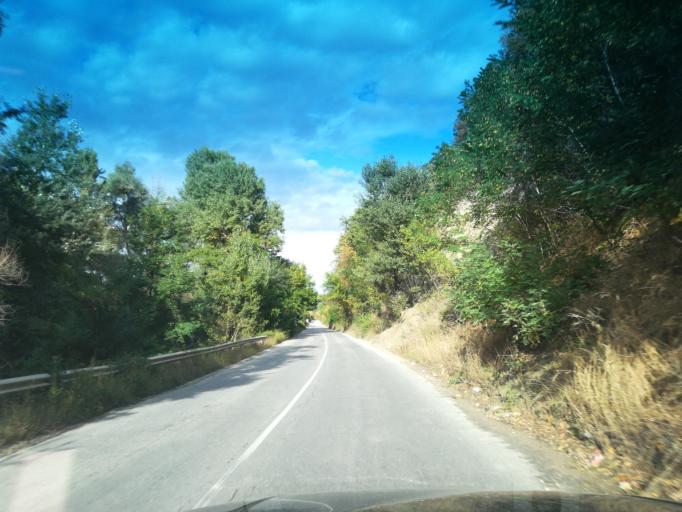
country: BG
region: Pazardzhik
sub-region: Obshtina Bratsigovo
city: Bratsigovo
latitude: 42.0532
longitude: 24.3414
